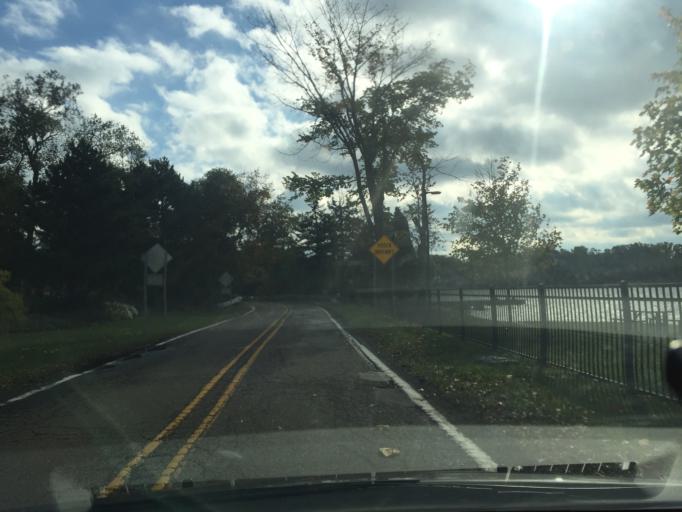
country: US
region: Michigan
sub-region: Oakland County
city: Keego Harbor
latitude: 42.5950
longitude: -83.3332
